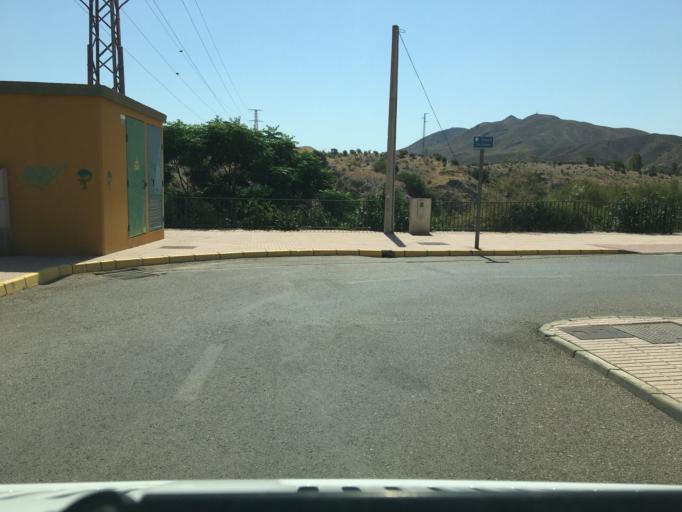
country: ES
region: Andalusia
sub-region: Provincia de Almeria
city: Huercal-Overa
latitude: 37.3987
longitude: -1.9380
